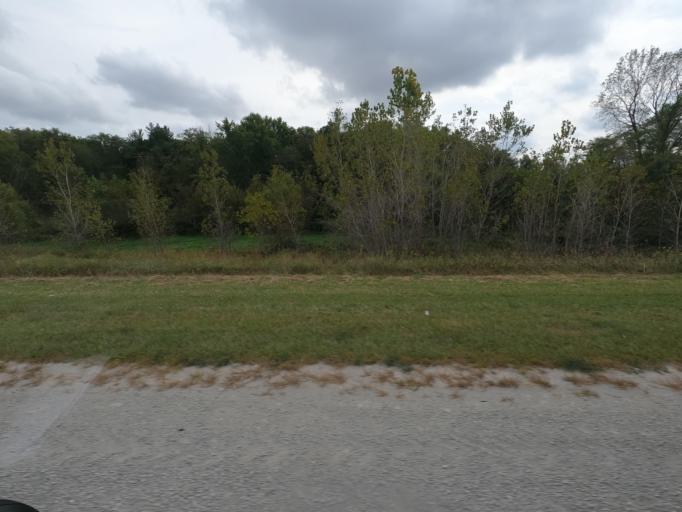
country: US
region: Iowa
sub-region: Wapello County
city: Ottumwa
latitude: 41.0030
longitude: -92.2791
